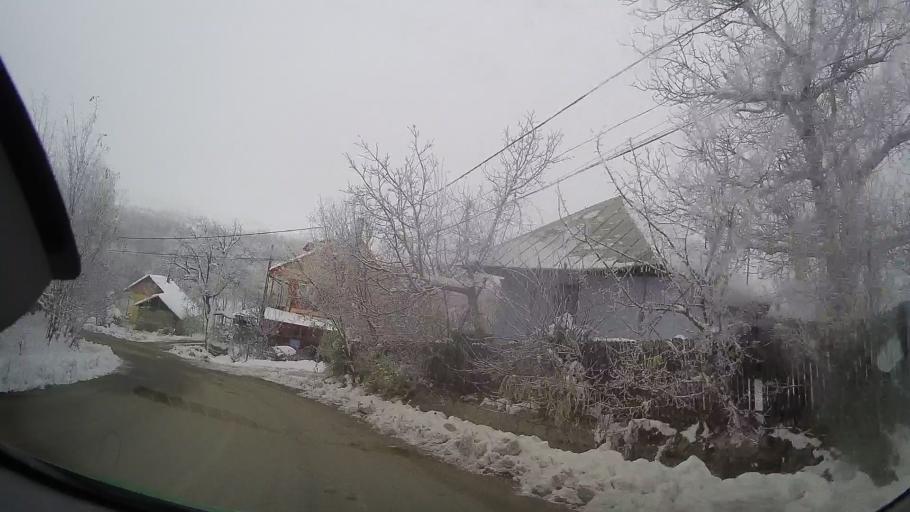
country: RO
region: Iasi
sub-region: Comuna Tansa
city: Suhulet
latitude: 46.8955
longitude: 27.2805
